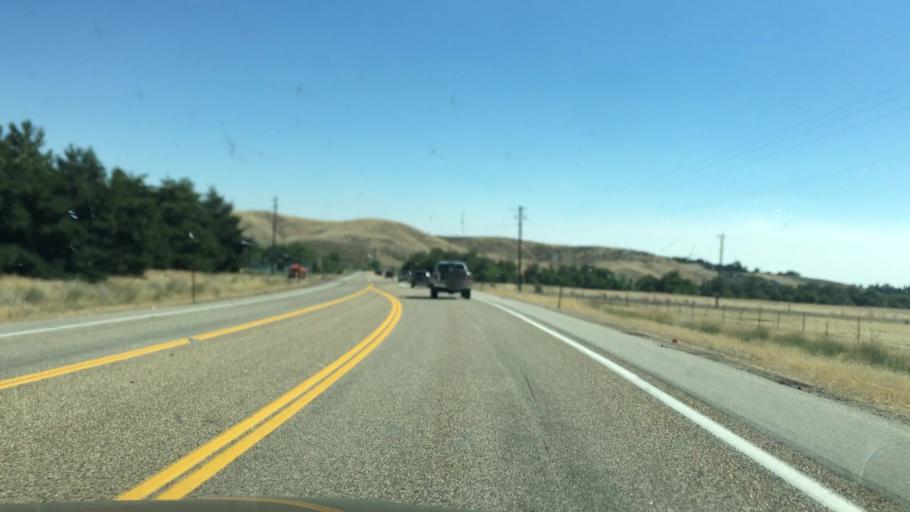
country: US
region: Idaho
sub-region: Ada County
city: Eagle
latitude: 43.7366
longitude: -116.3041
